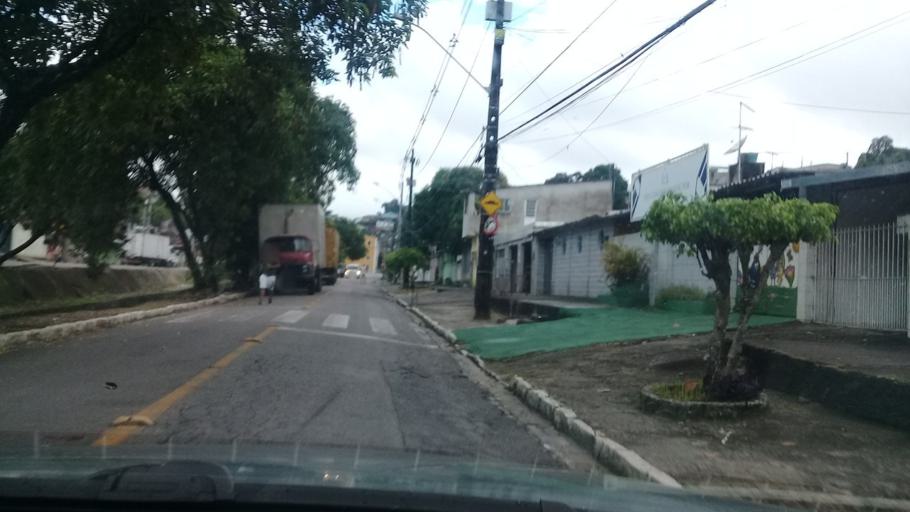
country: BR
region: Pernambuco
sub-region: Jaboatao Dos Guararapes
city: Jaboatao dos Guararapes
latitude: -8.1235
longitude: -34.9502
